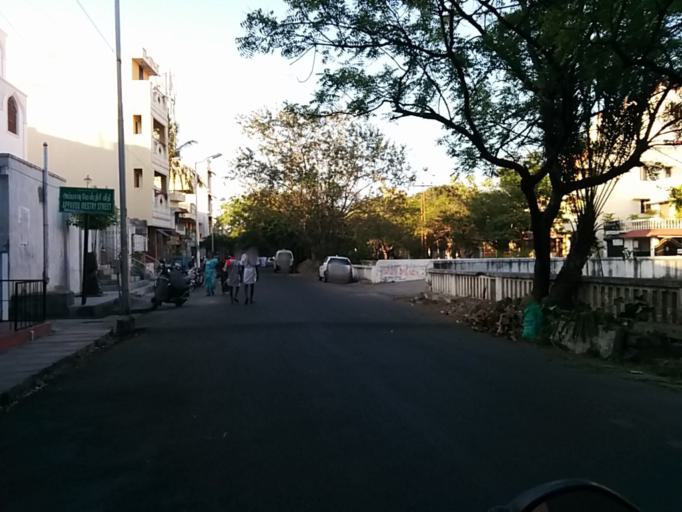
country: IN
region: Pondicherry
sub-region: Puducherry
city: Puducherry
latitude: 11.9261
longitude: 79.8310
